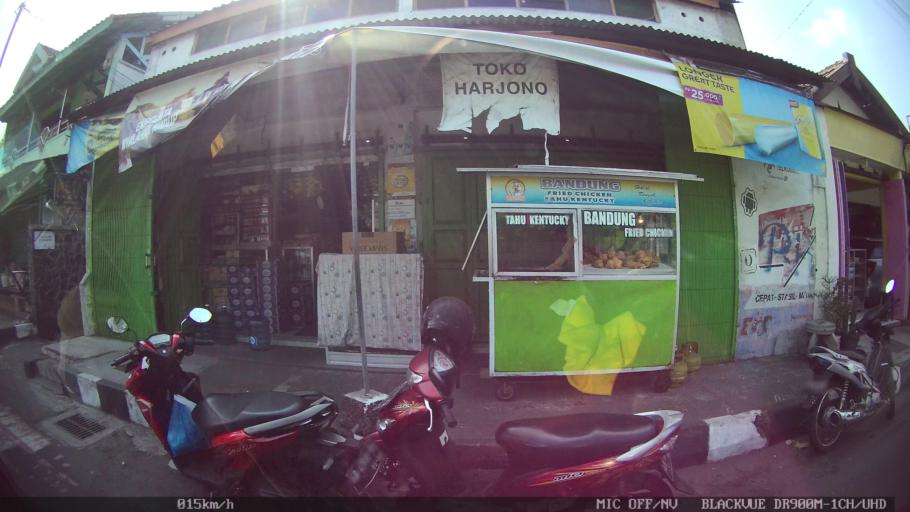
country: ID
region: Daerah Istimewa Yogyakarta
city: Yogyakarta
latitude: -7.8105
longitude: 110.3721
